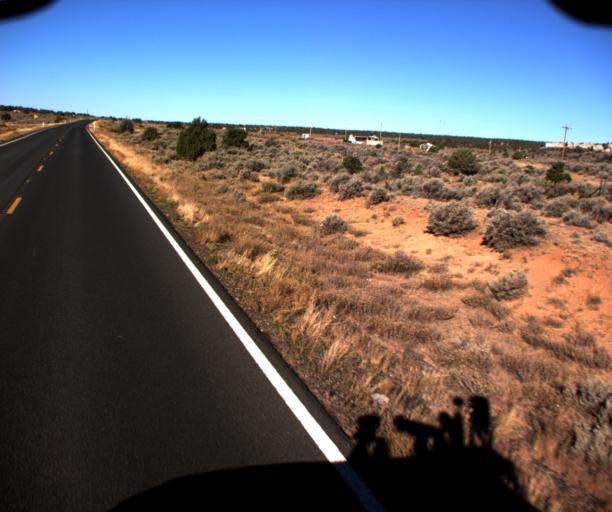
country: US
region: Arizona
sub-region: Apache County
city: Ganado
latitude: 35.7604
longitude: -109.7685
